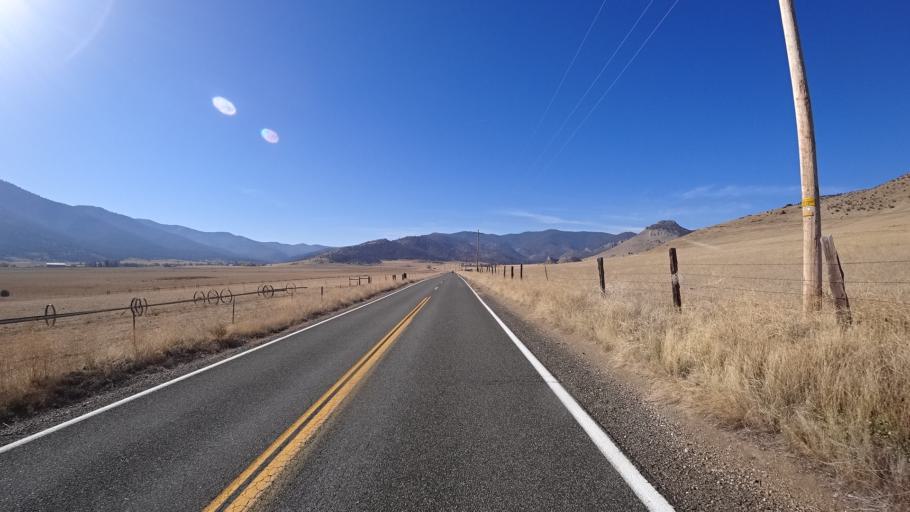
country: US
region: California
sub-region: Siskiyou County
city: Weed
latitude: 41.5076
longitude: -122.5364
